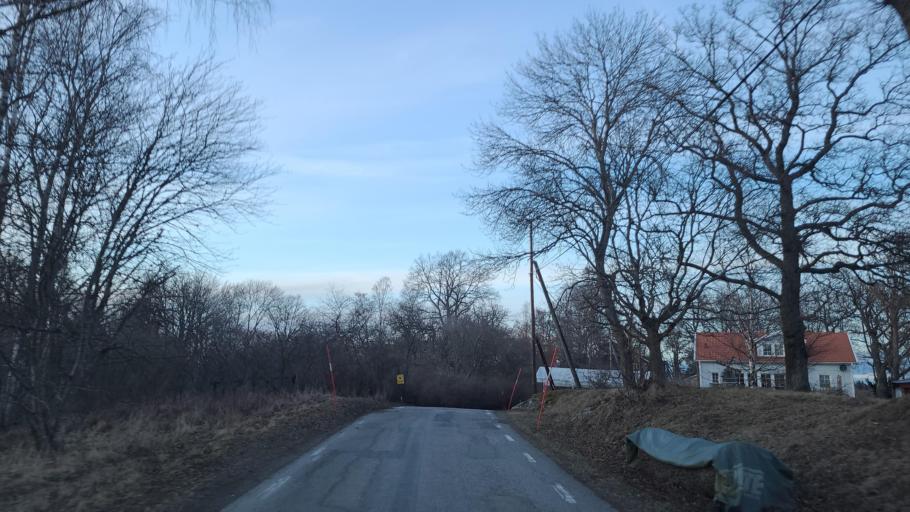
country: SE
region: Stockholm
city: Stenhamra
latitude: 59.4163
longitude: 17.6634
